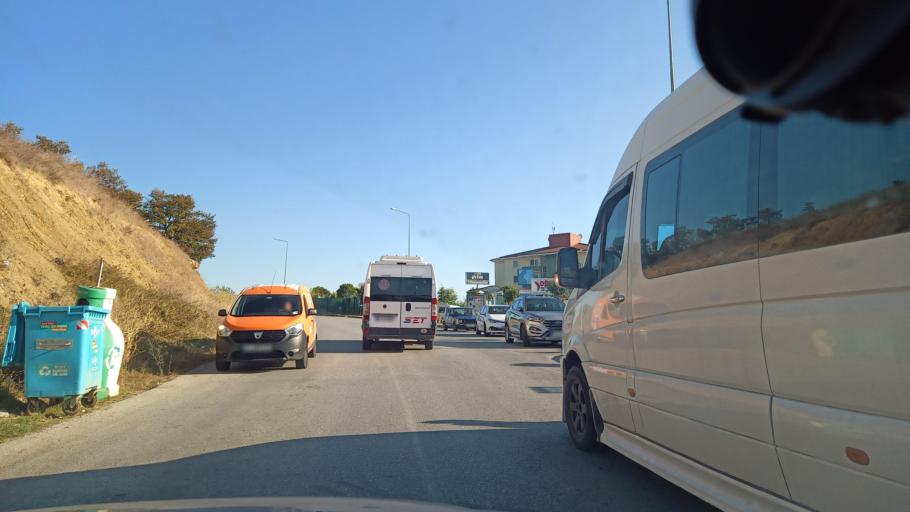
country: TR
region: Sakarya
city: Kazimpasa
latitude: 40.8556
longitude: 30.2772
